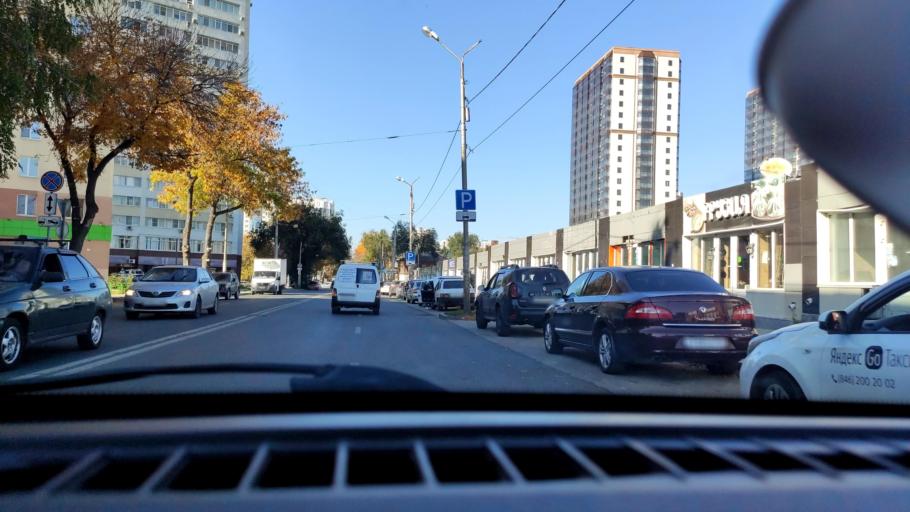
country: RU
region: Samara
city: Samara
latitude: 53.1962
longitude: 50.1242
